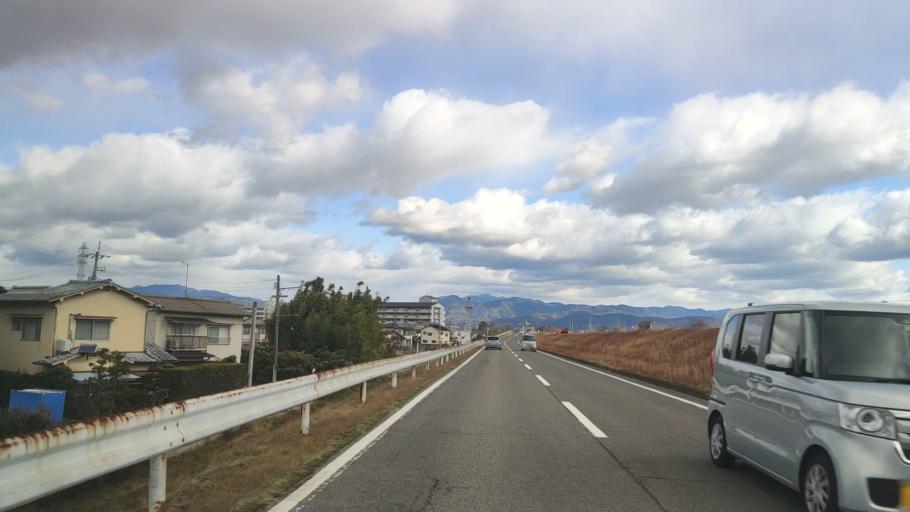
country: JP
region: Ehime
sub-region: Shikoku-chuo Shi
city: Matsuyama
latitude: 33.8126
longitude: 132.7450
